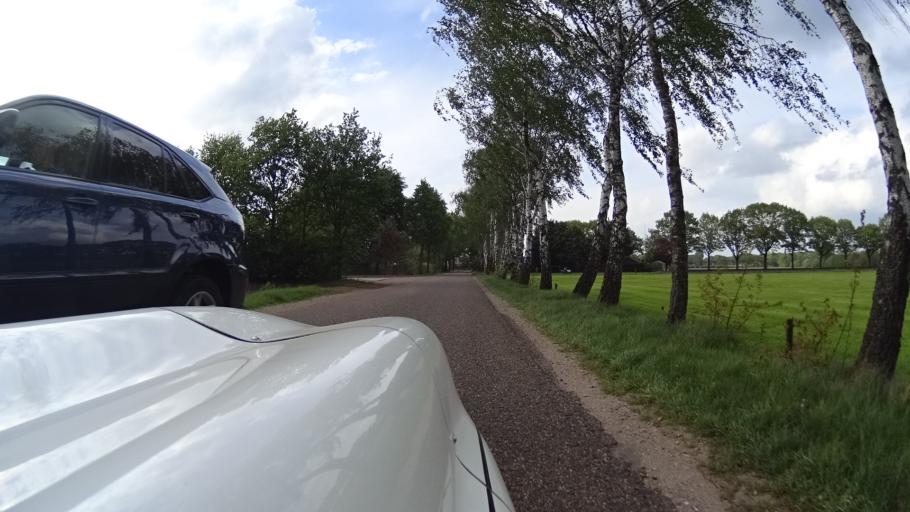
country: NL
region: North Brabant
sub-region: Gemeente Uden
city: Odiliapeel
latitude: 51.6336
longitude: 5.7235
